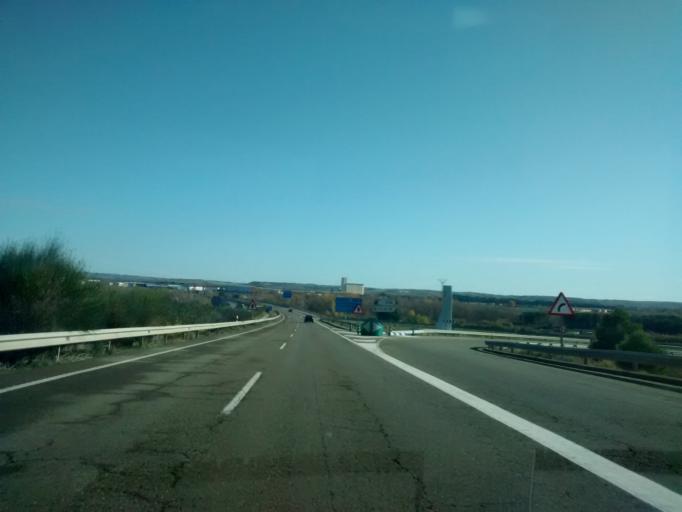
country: ES
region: Aragon
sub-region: Provincia de Zaragoza
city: Zuera
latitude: 41.8787
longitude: -0.7846
